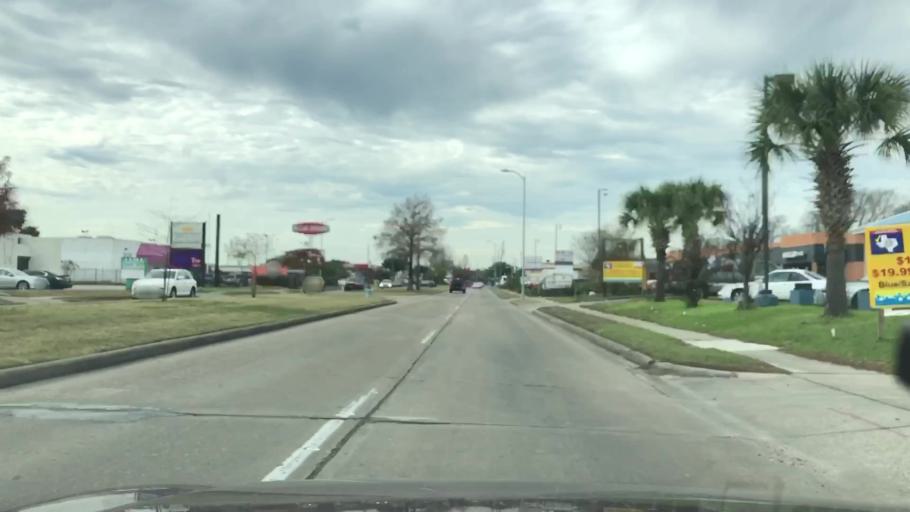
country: US
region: Texas
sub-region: Fort Bend County
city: Missouri City
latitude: 29.6559
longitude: -95.5249
